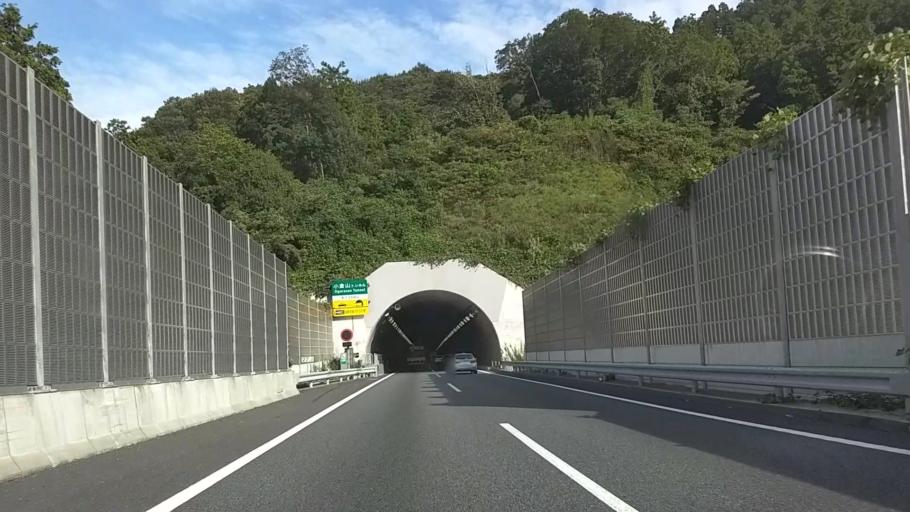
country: JP
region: Tokyo
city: Hachioji
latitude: 35.5594
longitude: 139.3123
